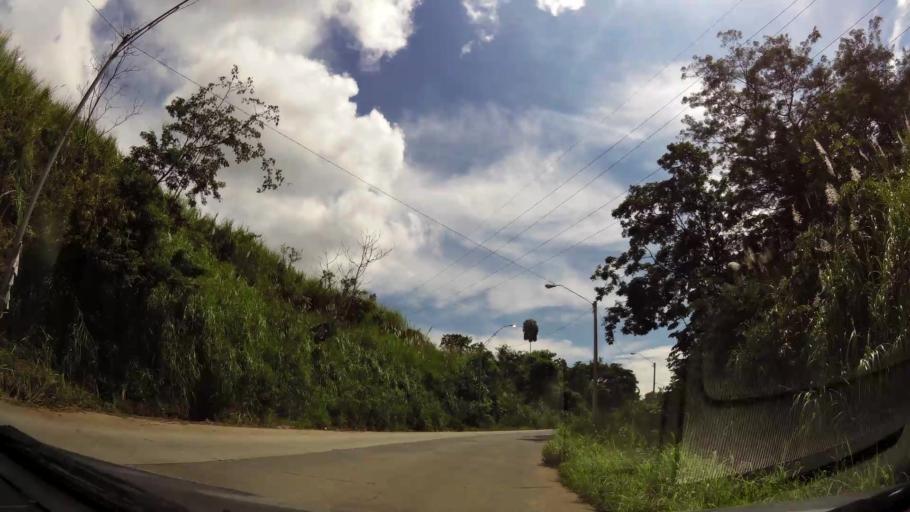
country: PA
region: Panama
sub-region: Distrito Arraijan
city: Arraijan
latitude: 8.9507
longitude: -79.6635
